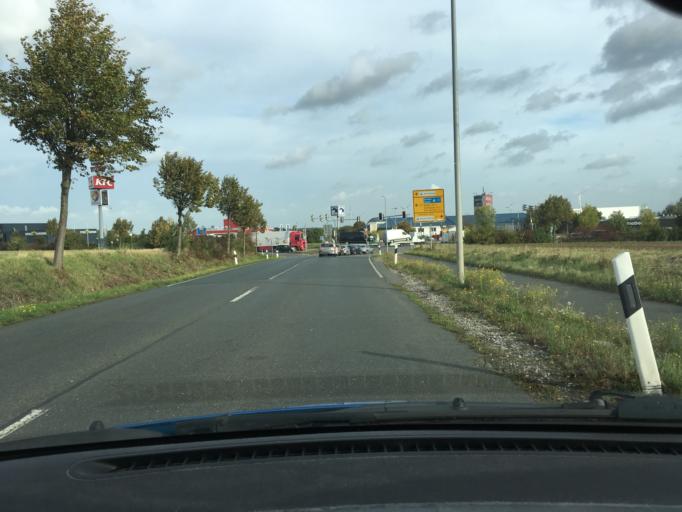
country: DE
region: Lower Saxony
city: Bad Nenndorf
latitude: 52.3321
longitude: 9.4125
